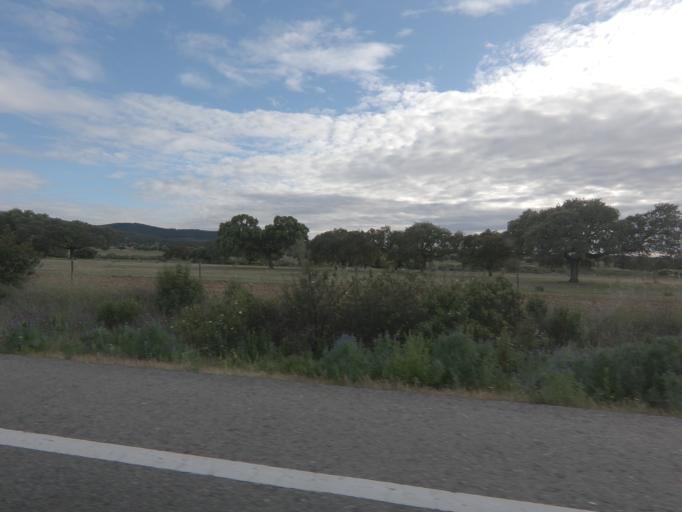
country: ES
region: Extremadura
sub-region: Provincia de Caceres
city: Pedroso de Acim
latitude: 39.8563
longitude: -6.4238
